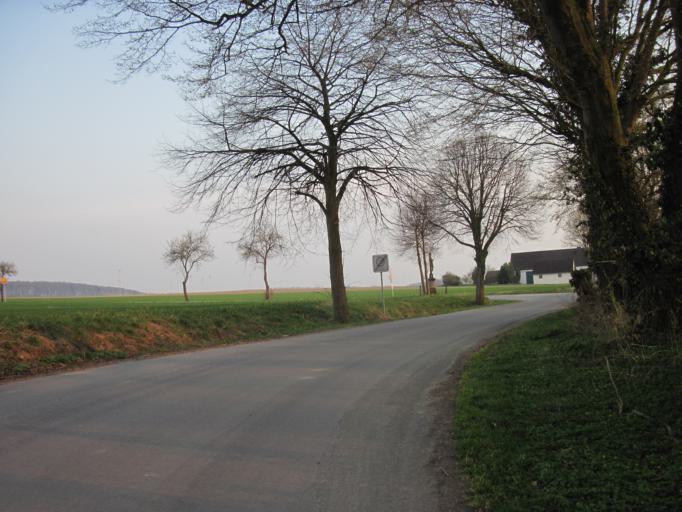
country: DE
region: North Rhine-Westphalia
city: Lichtenau
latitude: 51.6650
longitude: 8.8402
